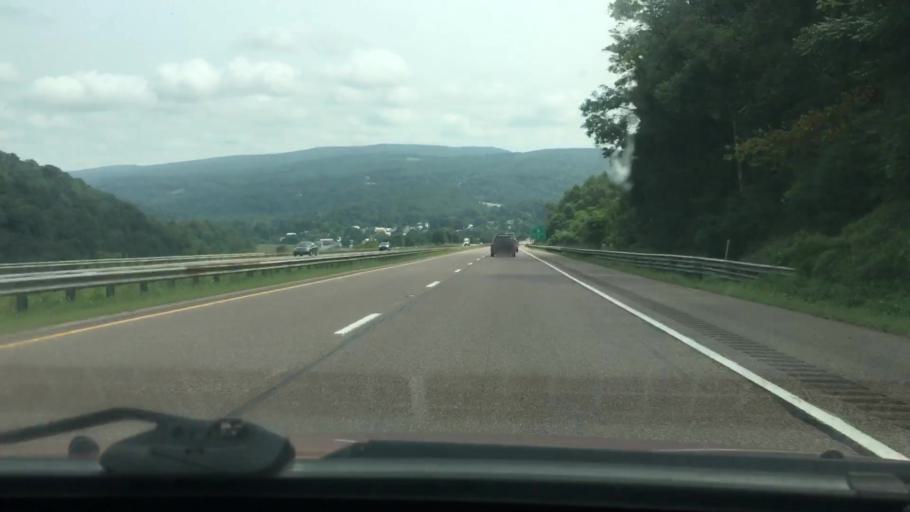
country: US
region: West Virginia
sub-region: Preston County
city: Terra Alta
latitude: 39.6621
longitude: -79.4223
